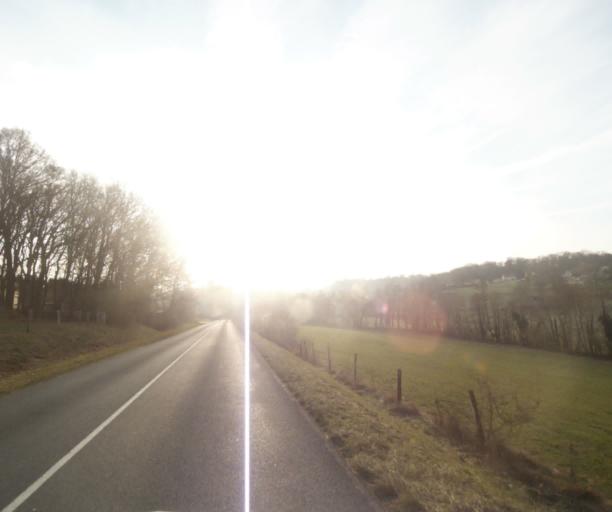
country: FR
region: Champagne-Ardenne
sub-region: Departement de la Marne
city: Sermaize-les-Bains
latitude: 48.7248
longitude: 4.9387
